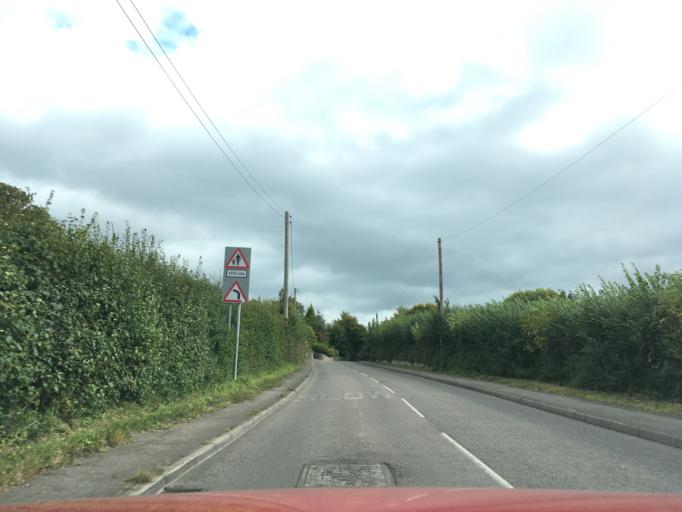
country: GB
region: England
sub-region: South Gloucestershire
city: Almondsbury
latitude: 51.5783
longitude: -2.5752
